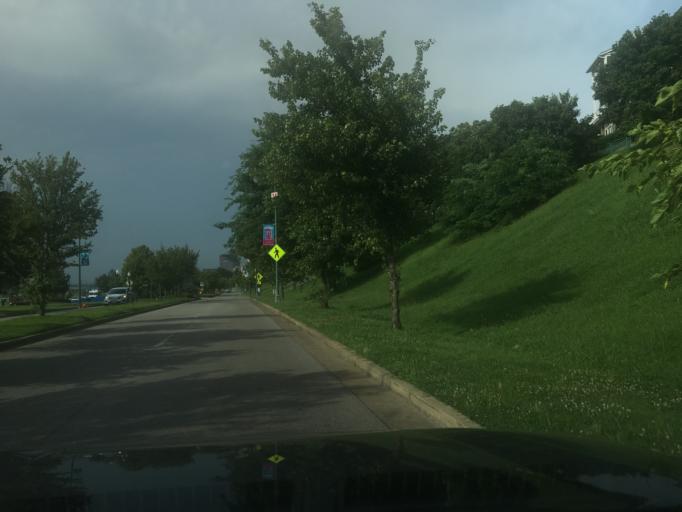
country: US
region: Tennessee
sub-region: Shelby County
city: Memphis
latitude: 35.1342
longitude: -90.0643
